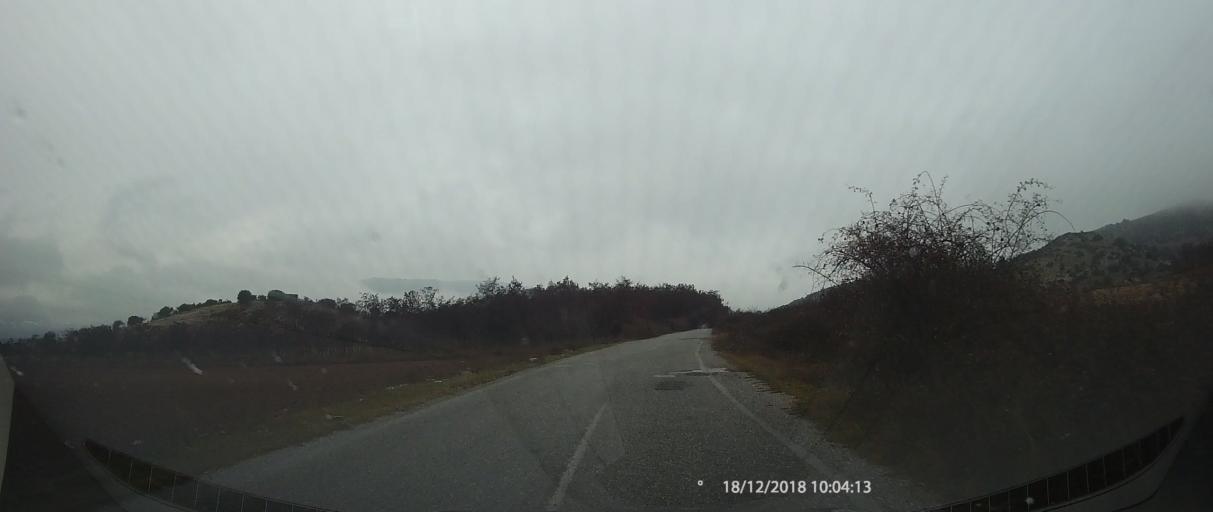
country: GR
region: Thessaly
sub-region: Nomos Larisis
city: Livadi
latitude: 40.0503
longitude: 22.2228
